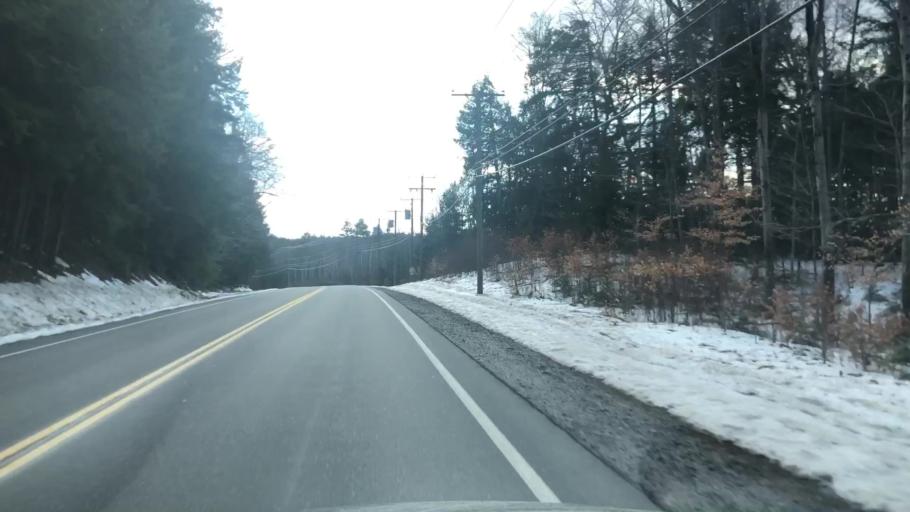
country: US
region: New Hampshire
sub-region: Hillsborough County
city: Mont Vernon
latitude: 42.8708
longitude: -71.6691
